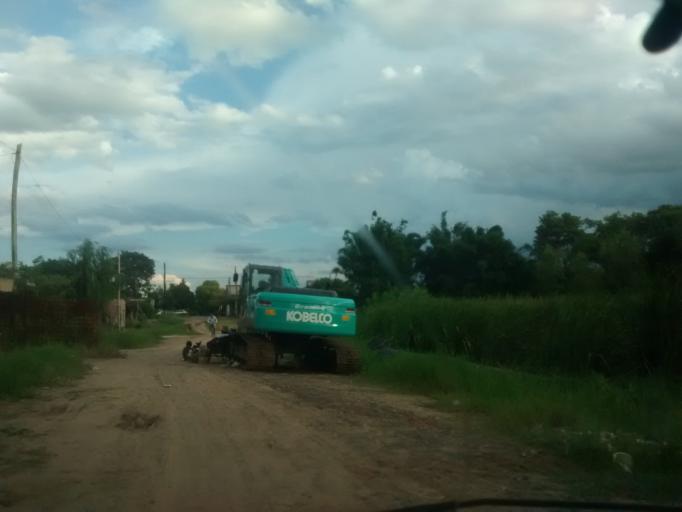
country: AR
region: Chaco
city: Fontana
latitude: -27.4299
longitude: -58.9985
